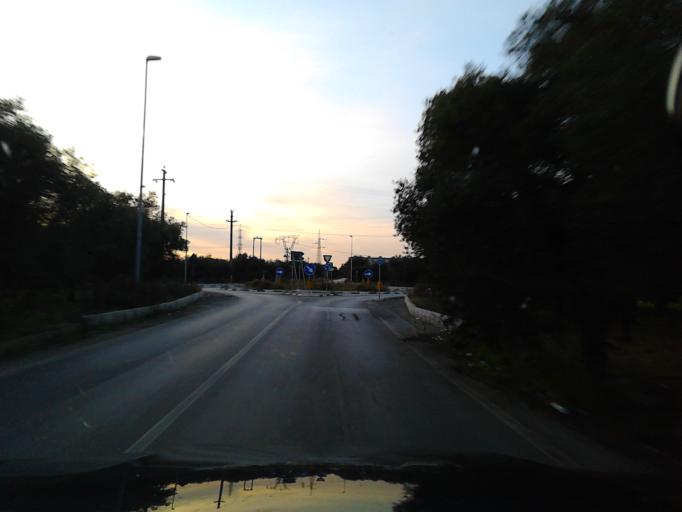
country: IT
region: Apulia
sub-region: Provincia di Bari
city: Lamie
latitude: 41.0397
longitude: 16.8641
